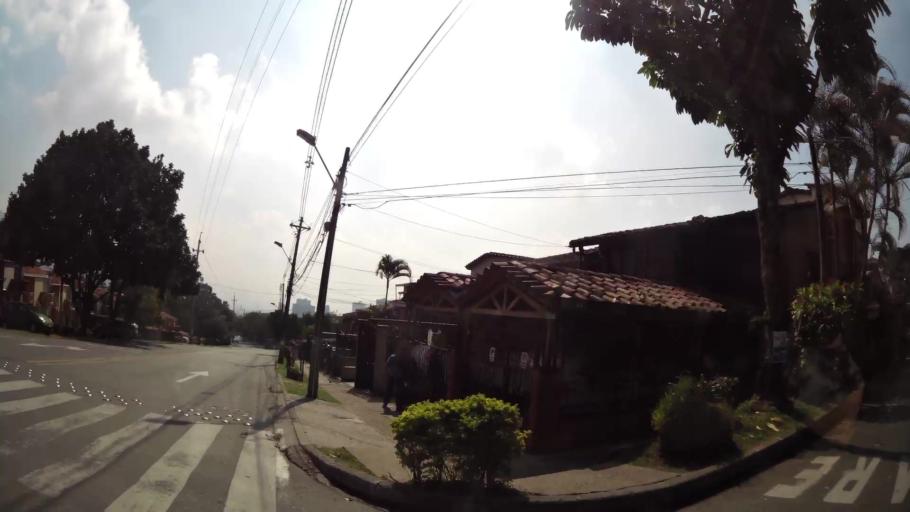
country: CO
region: Antioquia
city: La Estrella
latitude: 6.1683
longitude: -75.6431
